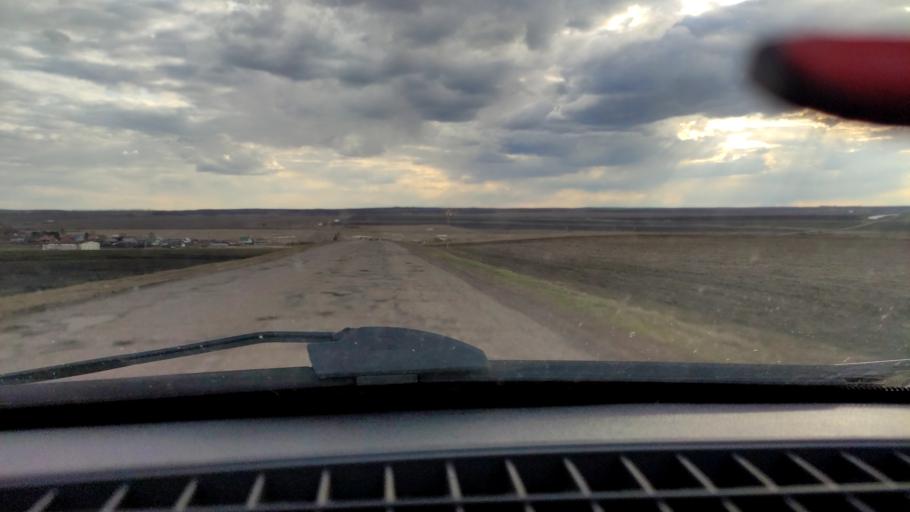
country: RU
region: Bashkortostan
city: Tolbazy
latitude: 54.2938
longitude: 55.9124
